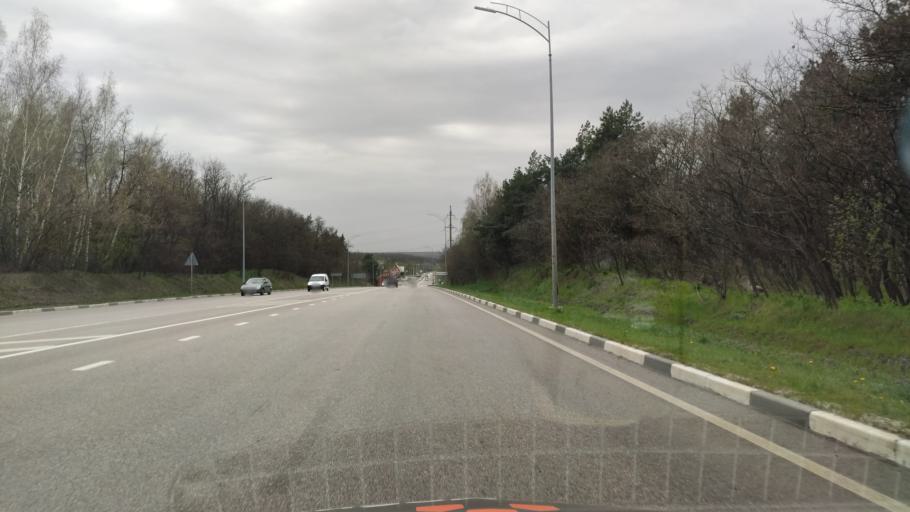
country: RU
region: Belgorod
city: Staryy Oskol
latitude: 51.3594
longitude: 37.8358
